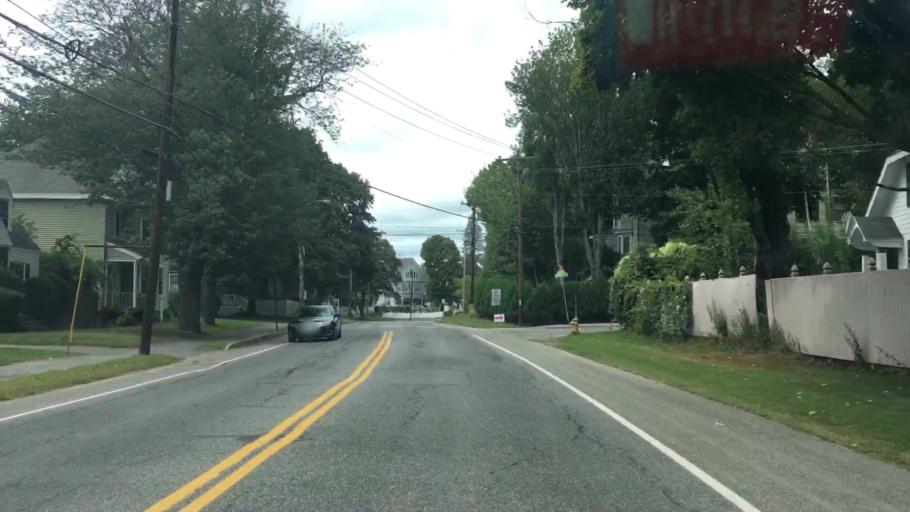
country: US
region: Maine
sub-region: Cumberland County
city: Westbrook
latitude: 43.6754
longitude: -70.3575
